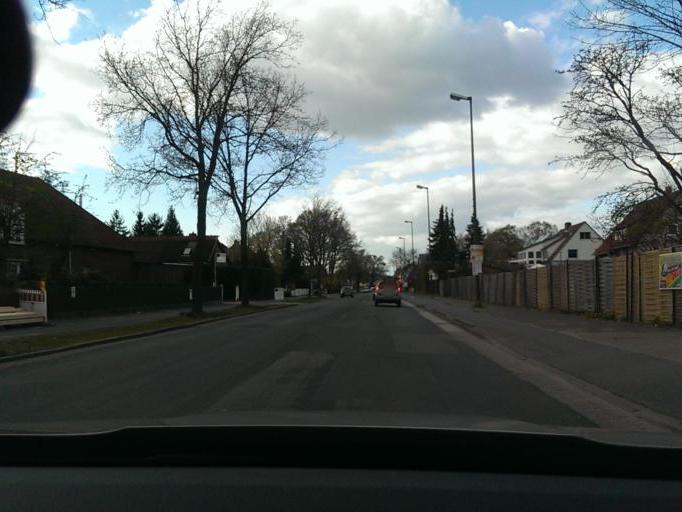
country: DE
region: Lower Saxony
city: Langenhagen
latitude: 52.4586
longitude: 9.7428
